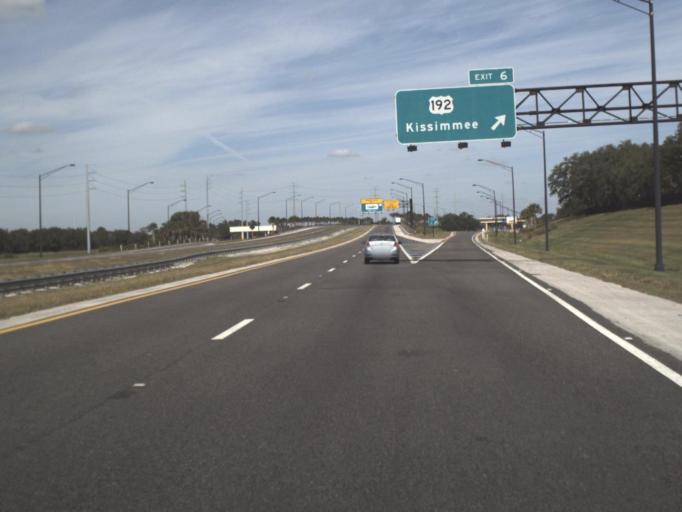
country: US
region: Florida
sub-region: Polk County
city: Citrus Ridge
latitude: 28.3401
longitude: -81.6157
